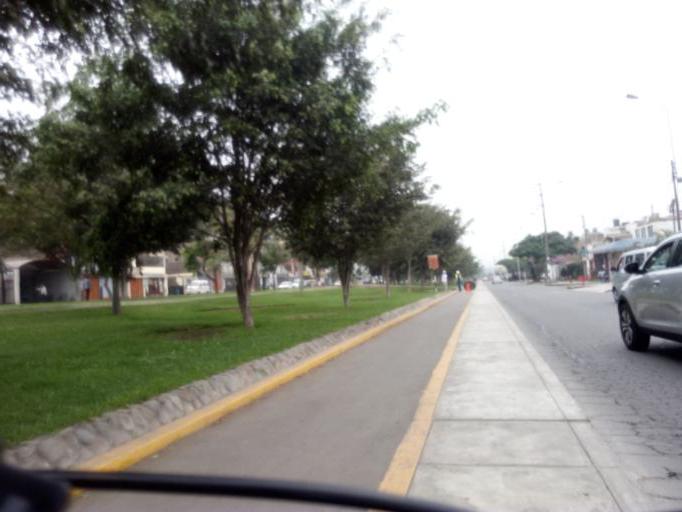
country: PE
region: Lima
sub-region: Lima
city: La Molina
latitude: -12.0579
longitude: -76.9440
